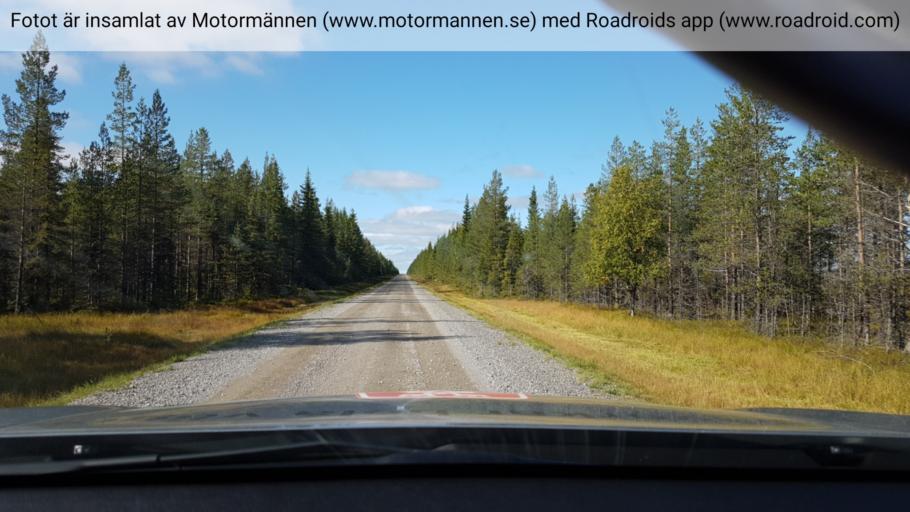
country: SE
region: Vaesterbotten
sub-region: Mala Kommun
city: Mala
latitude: 65.2251
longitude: 18.9957
